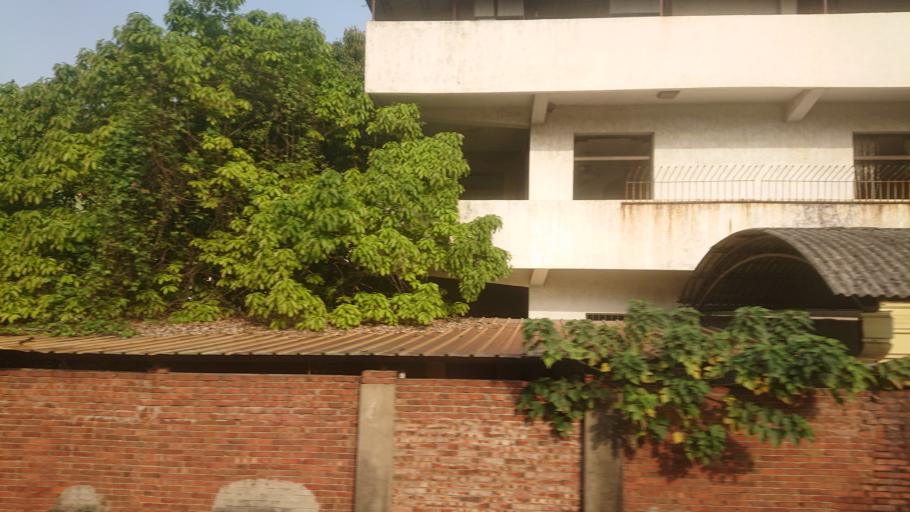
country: TW
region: Taiwan
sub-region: Yunlin
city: Douliu
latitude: 23.7136
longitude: 120.5437
